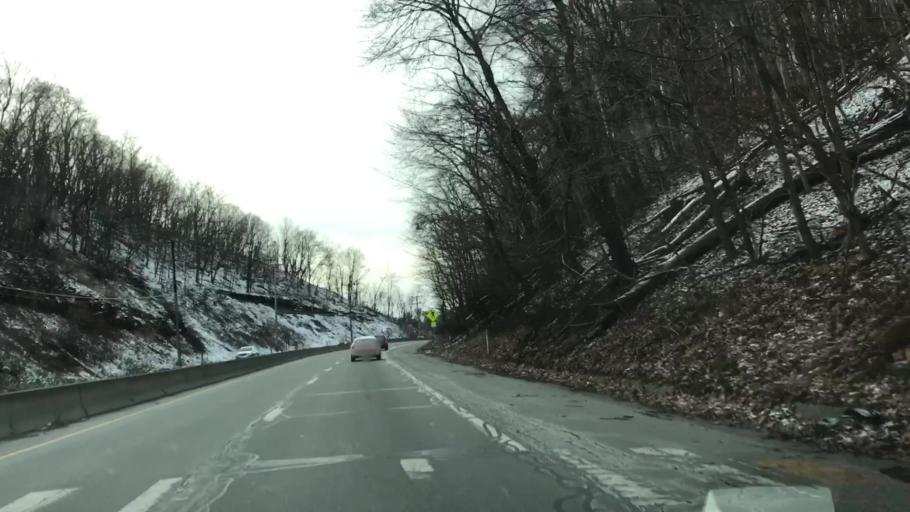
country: US
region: Pennsylvania
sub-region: Allegheny County
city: West View
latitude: 40.5116
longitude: -80.0039
